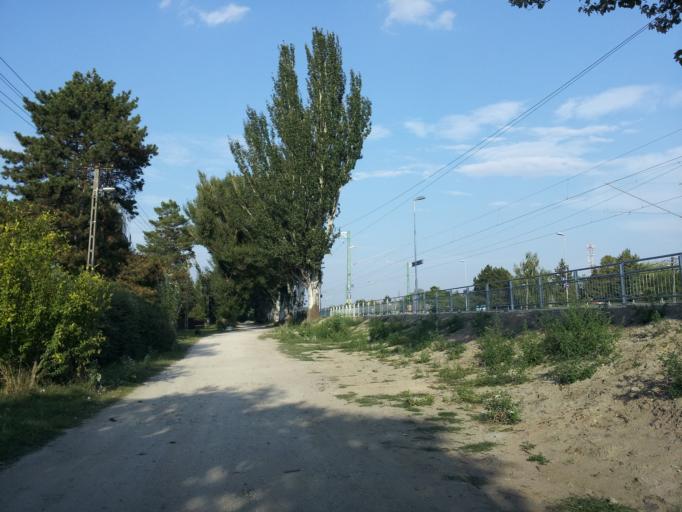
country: HU
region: Somogy
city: Zamardi
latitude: 46.8908
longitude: 17.9886
